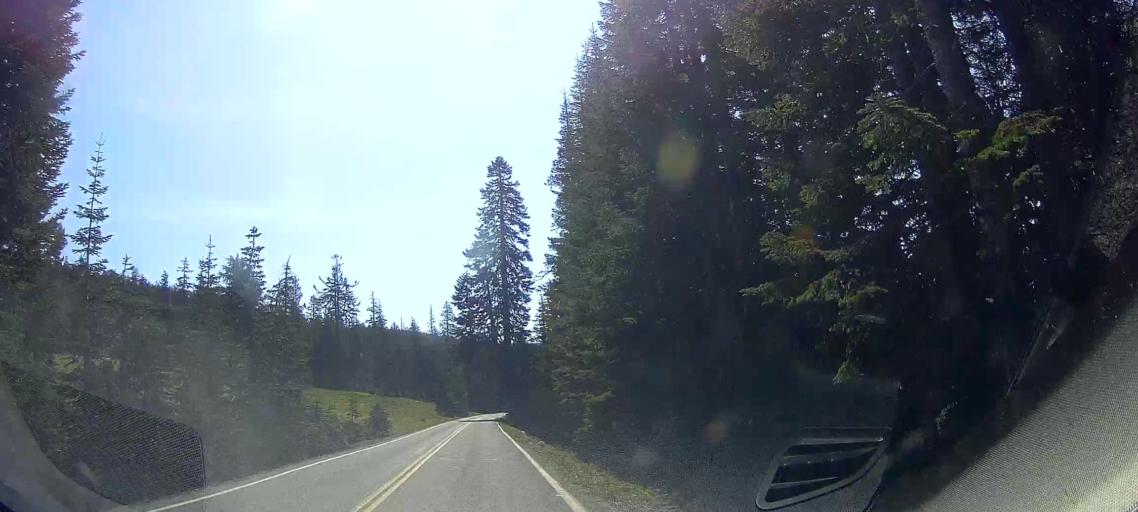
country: US
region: Oregon
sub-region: Klamath County
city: Klamath Falls
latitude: 42.8795
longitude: -122.1130
